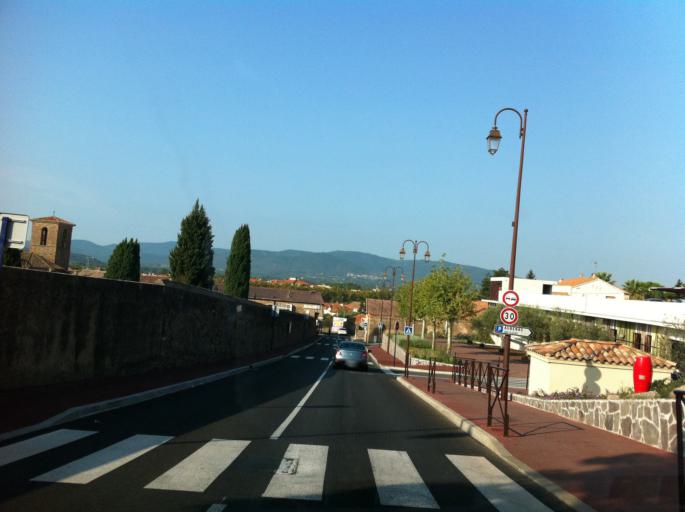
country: FR
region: Provence-Alpes-Cote d'Azur
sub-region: Departement du Var
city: Frejus
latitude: 43.4342
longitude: 6.7344
